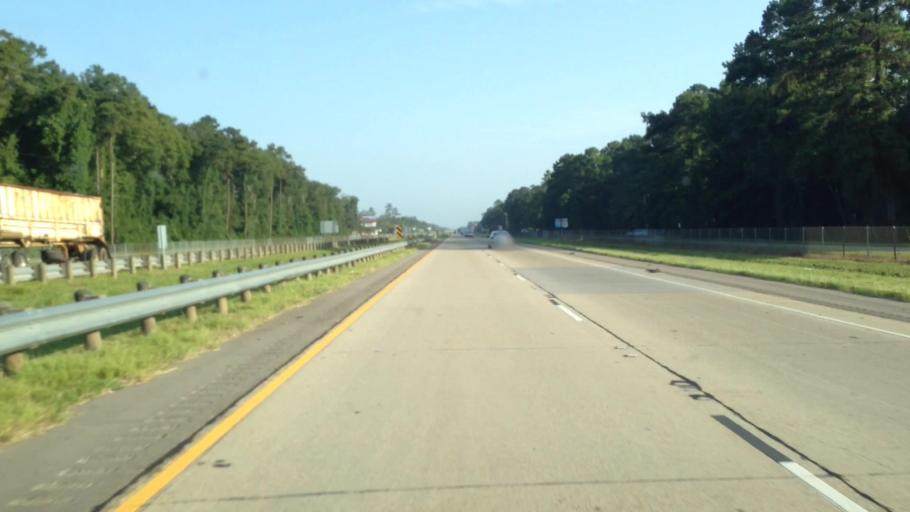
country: US
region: Louisiana
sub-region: Tangipahoa Parish
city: Ponchatoula
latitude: 30.4431
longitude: -90.4638
